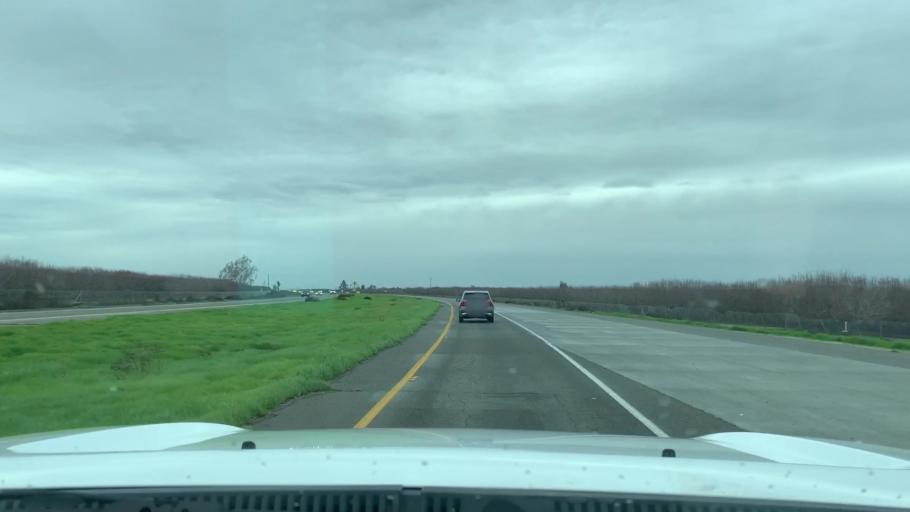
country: US
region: California
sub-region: Fresno County
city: Caruthers
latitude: 36.4962
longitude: -119.7866
